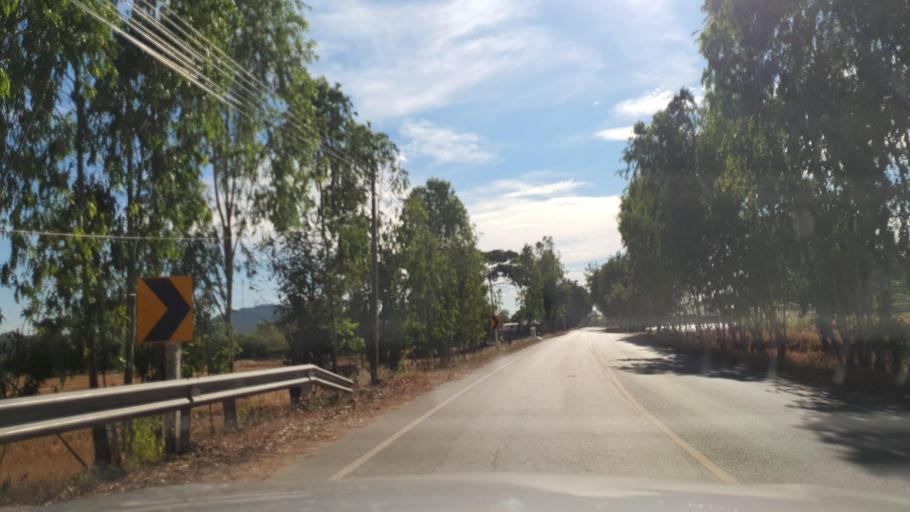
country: TH
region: Kalasin
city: Kuchinarai
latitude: 16.5951
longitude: 104.1345
